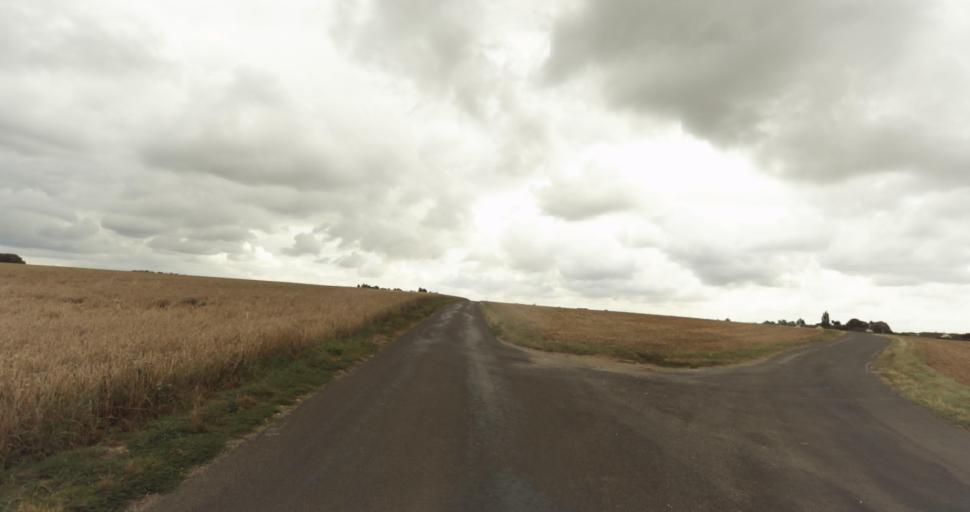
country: FR
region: Haute-Normandie
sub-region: Departement de l'Eure
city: Menilles
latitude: 49.0231
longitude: 1.2979
